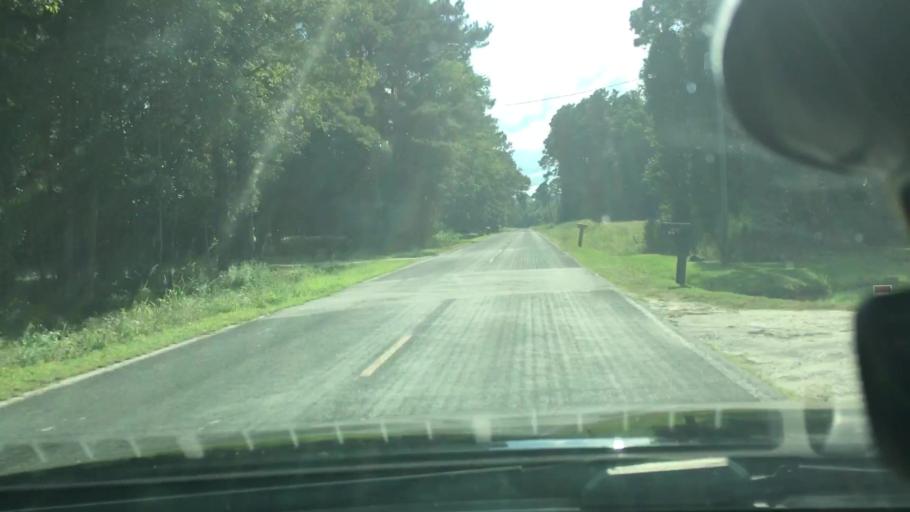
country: US
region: North Carolina
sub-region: Craven County
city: Vanceboro
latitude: 35.3349
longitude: -77.1656
